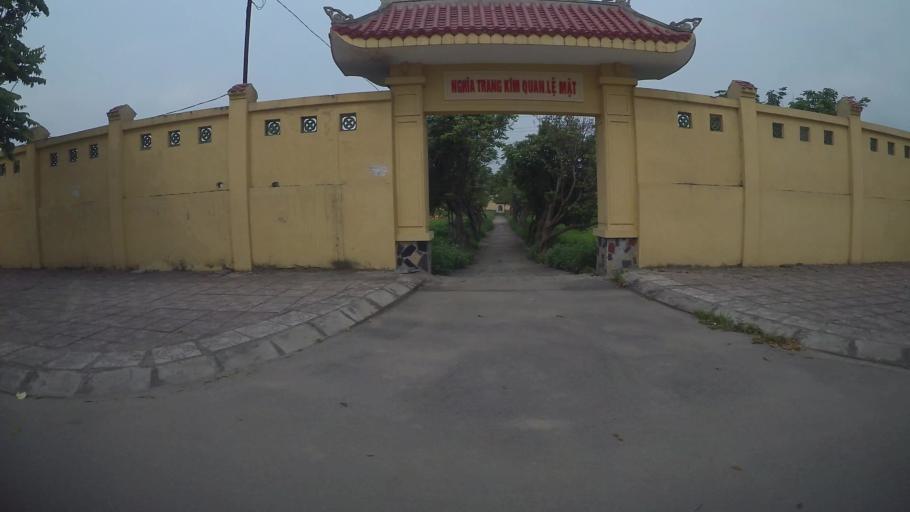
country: VN
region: Ha Noi
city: Trau Quy
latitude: 21.0560
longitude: 105.9033
